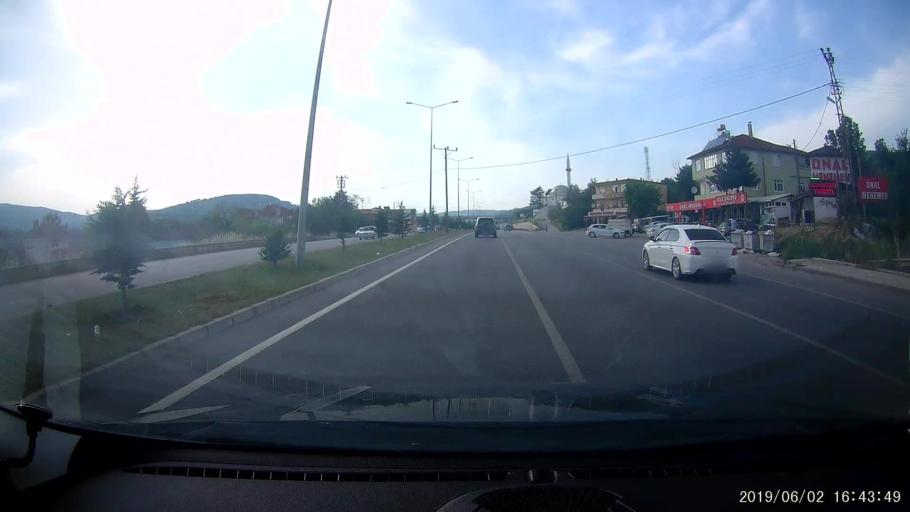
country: TR
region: Samsun
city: Kavak
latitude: 41.1413
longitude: 36.1202
